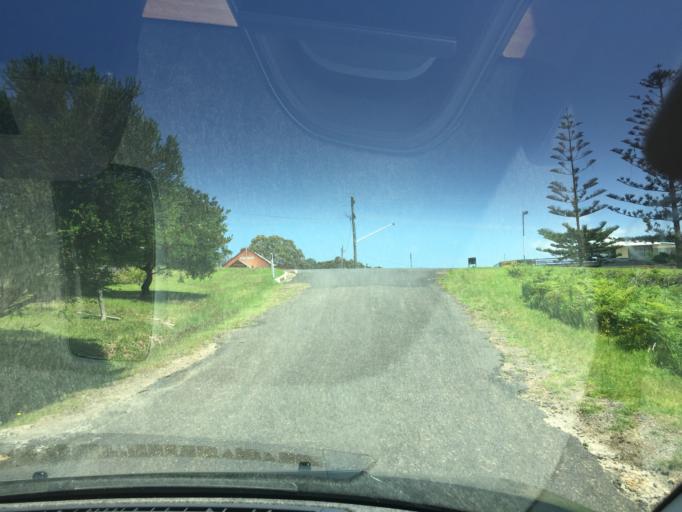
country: AU
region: New South Wales
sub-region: Bega Valley
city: Bega
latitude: -36.7291
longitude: 149.9877
